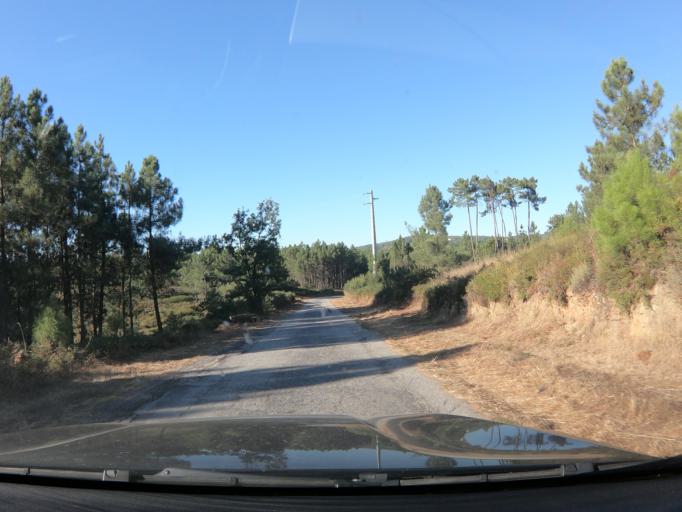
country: PT
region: Vila Real
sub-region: Sabrosa
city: Vilela
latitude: 41.2488
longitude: -7.6284
